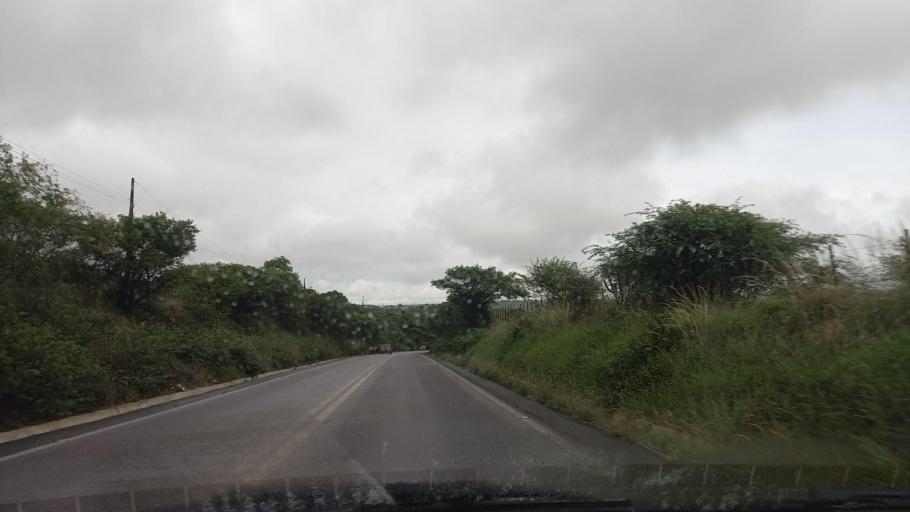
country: BR
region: Pernambuco
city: Garanhuns
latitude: -8.8488
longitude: -36.5190
